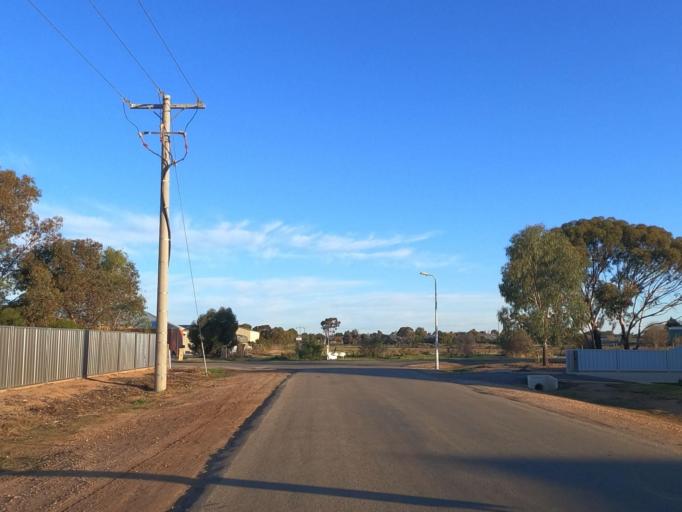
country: AU
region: Victoria
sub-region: Swan Hill
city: Swan Hill
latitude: -35.3325
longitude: 143.5342
